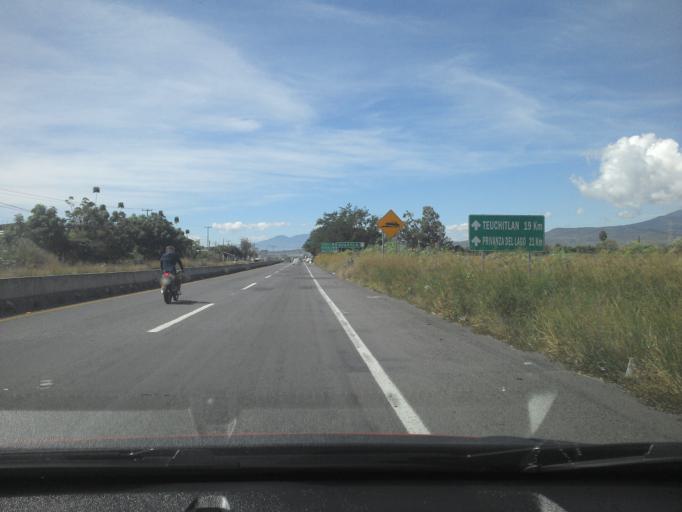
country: MX
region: Jalisco
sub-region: Tala
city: Los Ruisenores
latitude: 20.7142
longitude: -103.6506
